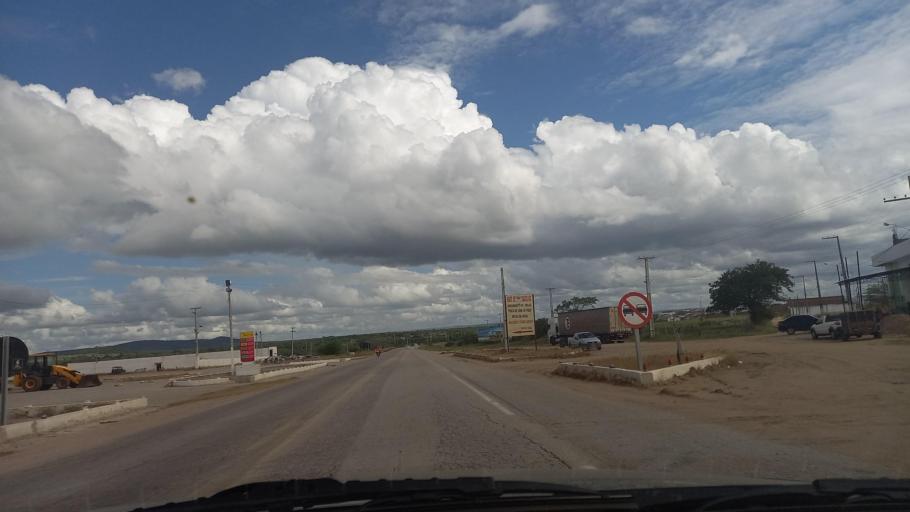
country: BR
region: Pernambuco
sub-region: Cachoeirinha
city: Cachoeirinha
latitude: -8.4803
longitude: -36.2242
